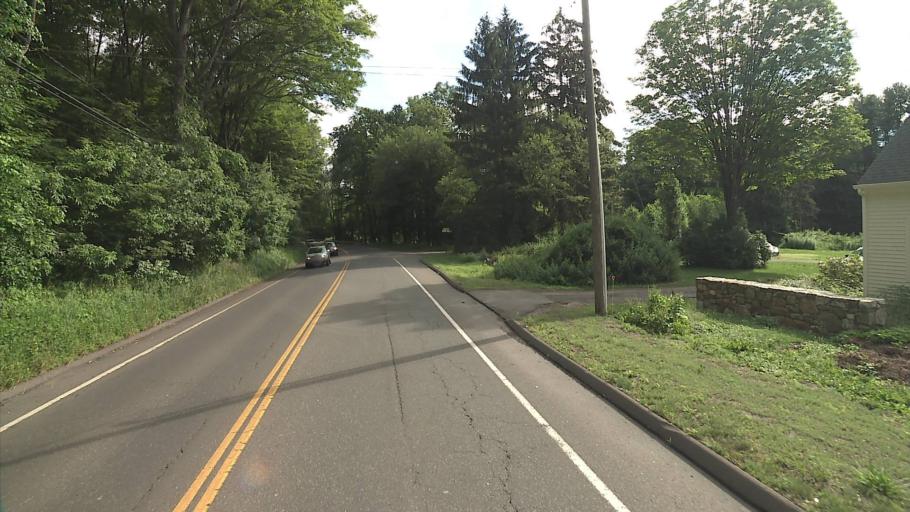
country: US
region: Connecticut
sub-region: New Haven County
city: Woodbridge
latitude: 41.3837
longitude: -73.0003
